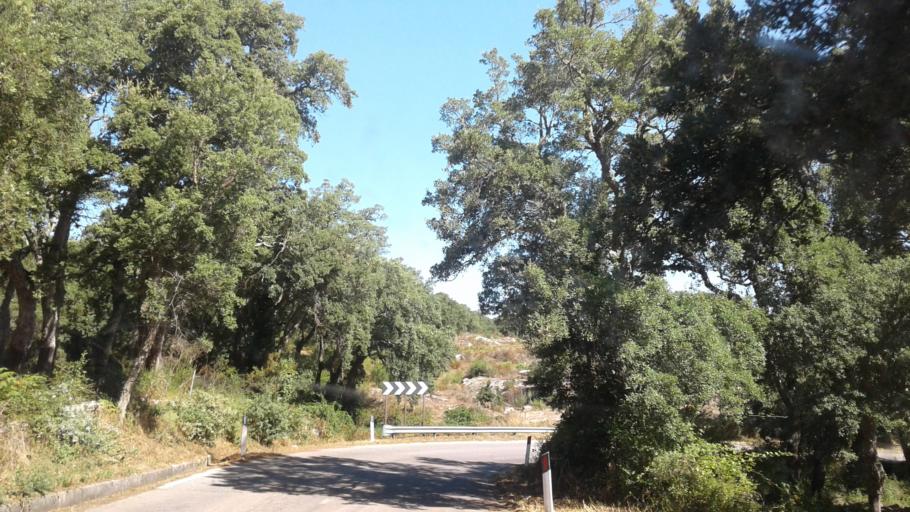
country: IT
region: Sardinia
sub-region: Provincia di Olbia-Tempio
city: Aggius
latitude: 40.9399
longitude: 9.0821
